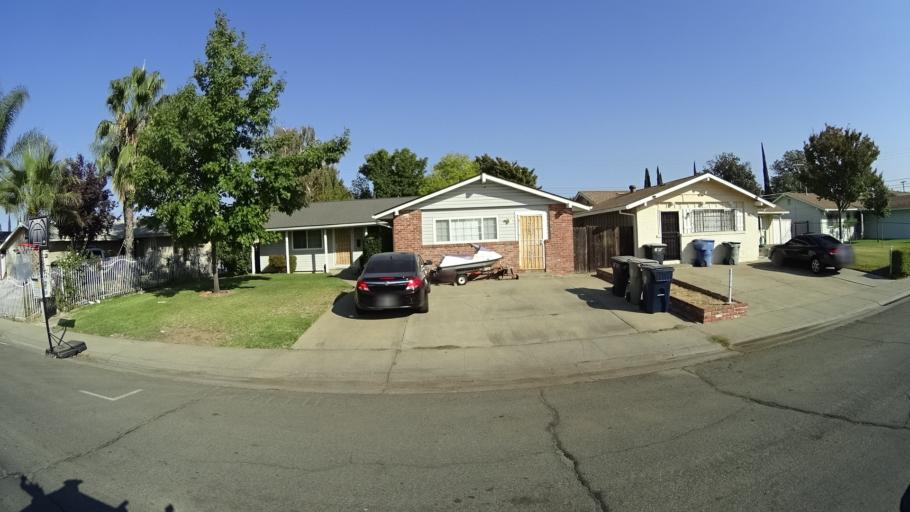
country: US
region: California
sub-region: Sacramento County
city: Parkway
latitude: 38.4773
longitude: -121.4832
